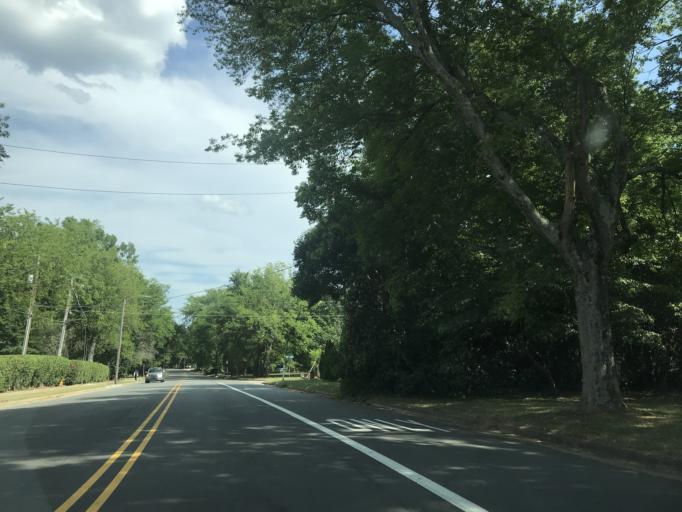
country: US
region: North Carolina
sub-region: Wake County
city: Raleigh
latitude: 35.7786
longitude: -78.6074
